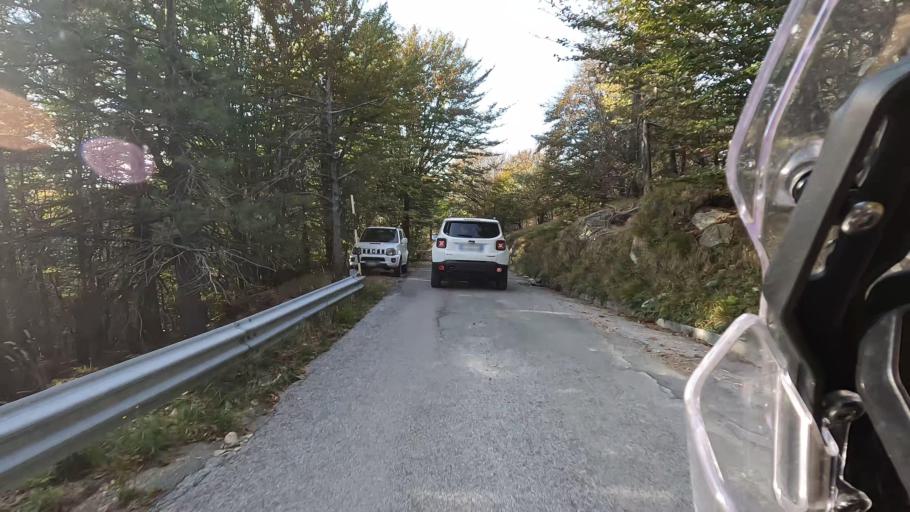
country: IT
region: Liguria
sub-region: Provincia di Savona
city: San Giovanni
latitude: 44.4298
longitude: 8.5462
